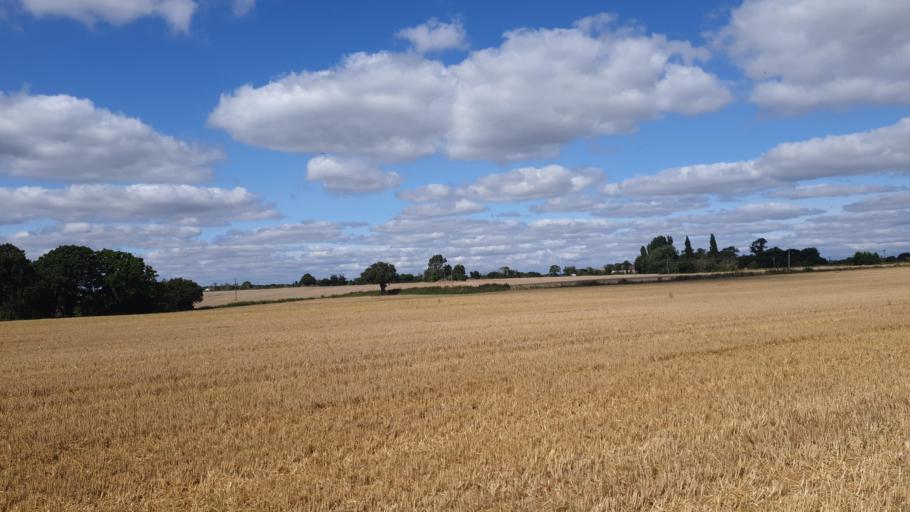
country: GB
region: England
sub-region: Essex
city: Dovercourt
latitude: 51.9125
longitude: 1.2183
